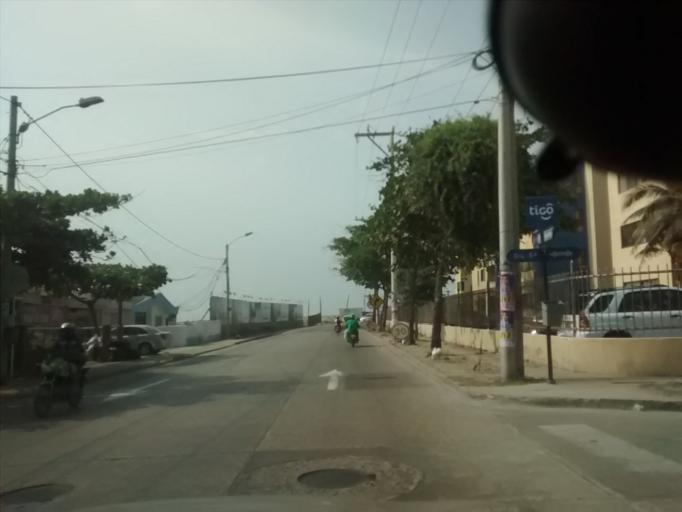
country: CO
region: Bolivar
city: Cartagena
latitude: 10.4493
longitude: -75.5172
